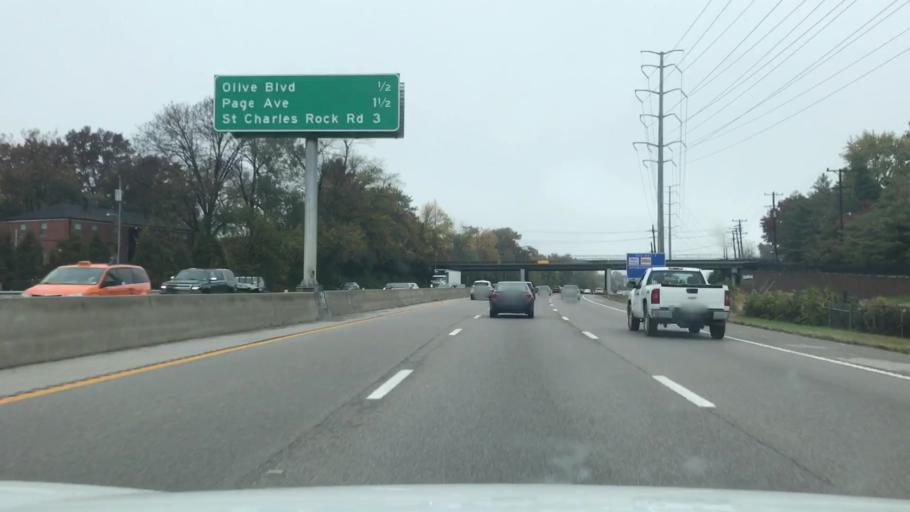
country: US
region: Missouri
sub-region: Saint Louis County
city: Olivette
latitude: 38.6664
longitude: -90.3606
